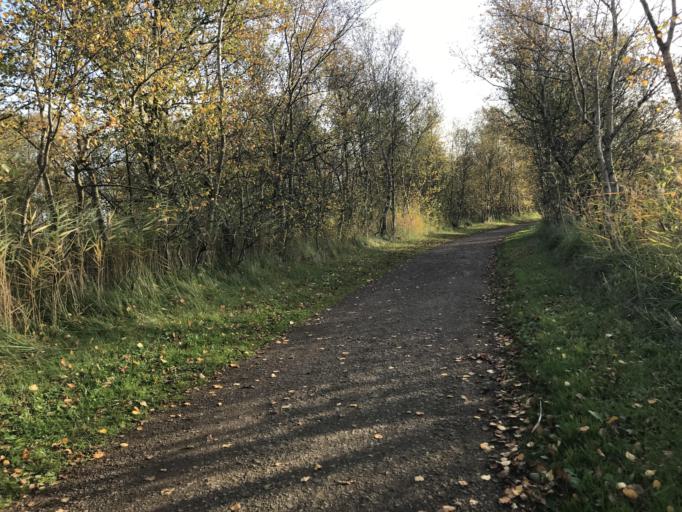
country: DE
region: Lower Saxony
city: Borkum
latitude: 53.5747
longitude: 6.7074
